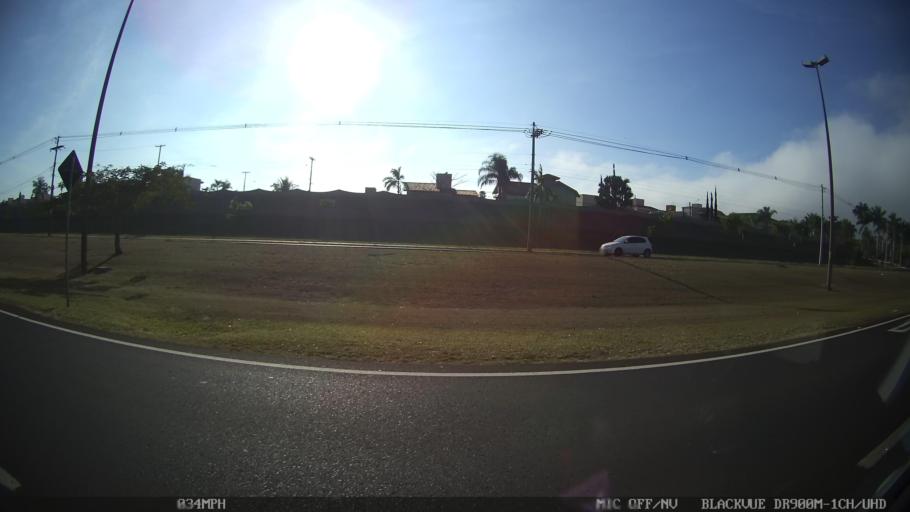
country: BR
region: Sao Paulo
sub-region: Sao Jose Do Rio Preto
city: Sao Jose do Rio Preto
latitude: -20.8195
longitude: -49.3461
